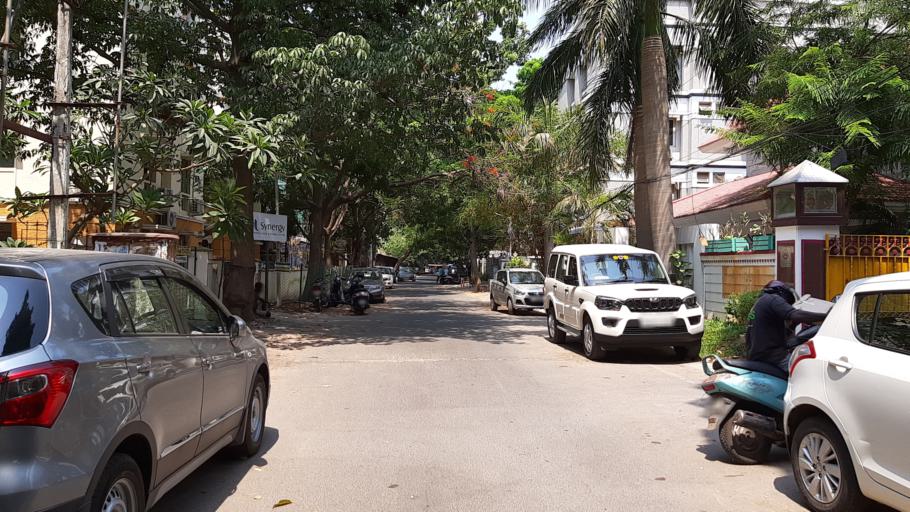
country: IN
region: Tamil Nadu
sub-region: Chennai
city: Chetput
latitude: 13.0472
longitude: 80.2405
